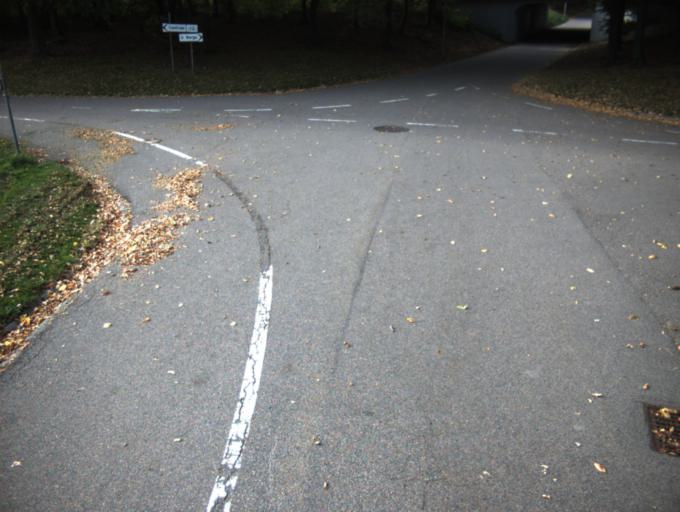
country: SE
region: Skane
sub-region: Helsingborg
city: Helsingborg
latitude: 56.0612
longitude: 12.7117
